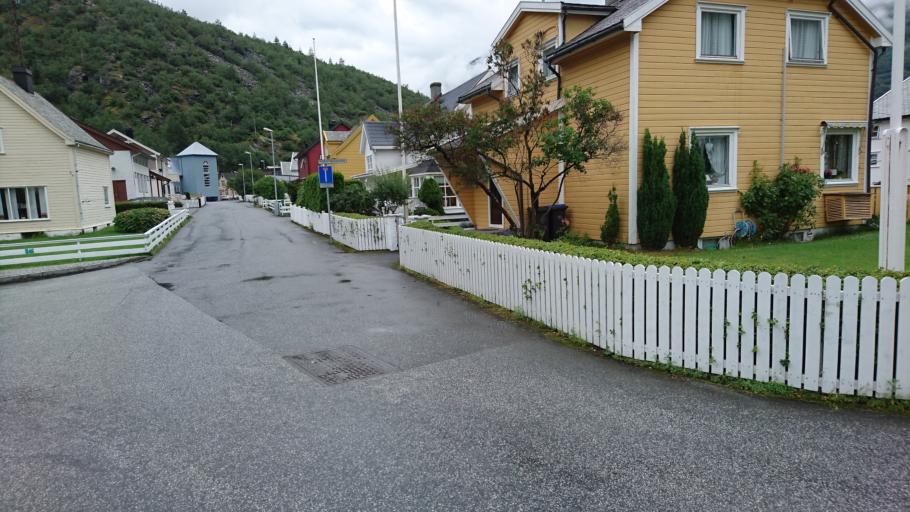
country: NO
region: Sogn og Fjordane
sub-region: Ardal
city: Farnes
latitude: 61.3095
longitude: 7.8018
